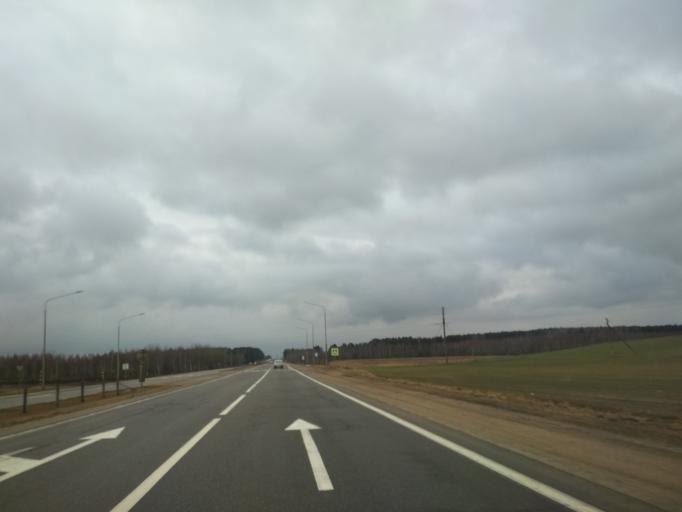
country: BY
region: Minsk
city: Luhavaya Slabada
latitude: 53.7239
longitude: 27.8597
